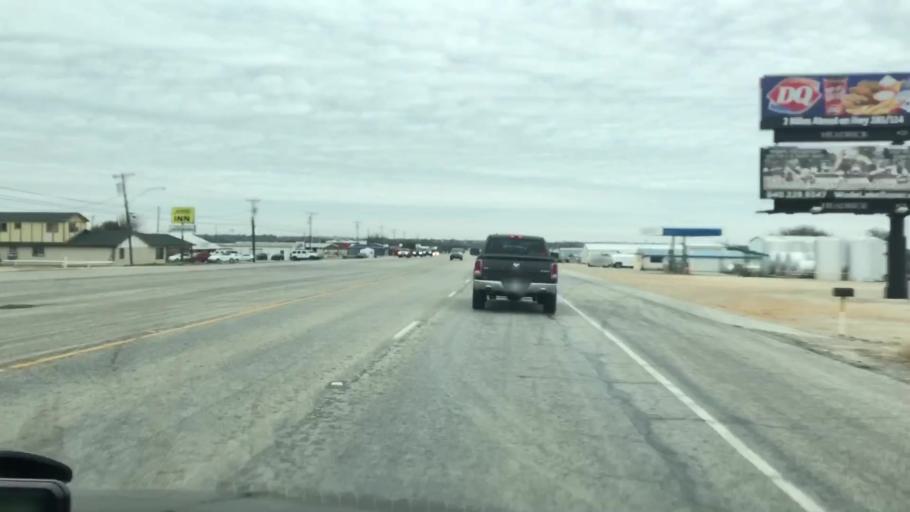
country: US
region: Texas
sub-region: Jack County
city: Jacksboro
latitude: 33.1999
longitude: -98.1486
